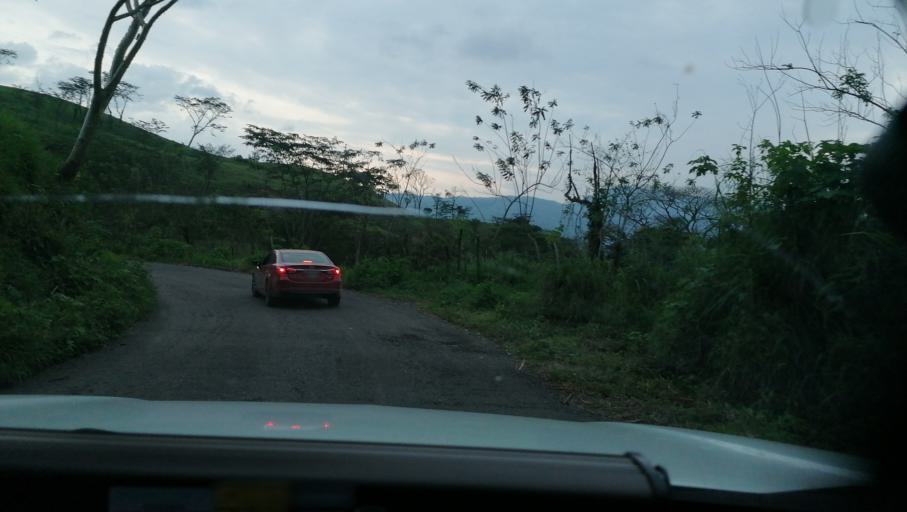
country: MX
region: Chiapas
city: Ixtacomitan
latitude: 17.3977
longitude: -93.0997
